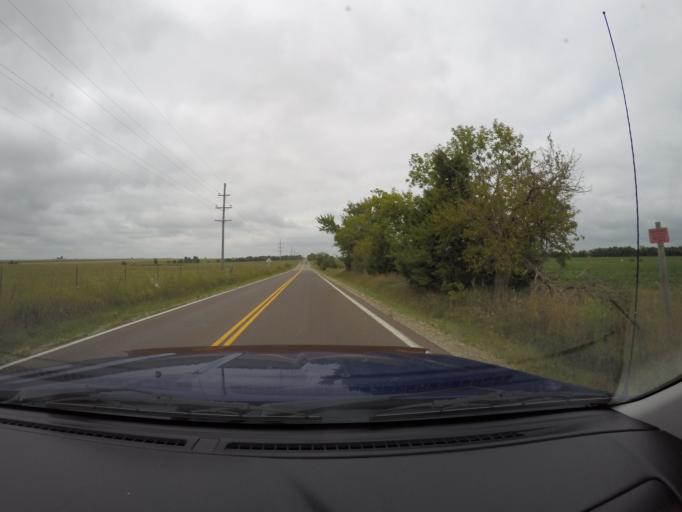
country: US
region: Kansas
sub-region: Morris County
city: Council Grove
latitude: 38.8571
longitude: -96.5939
